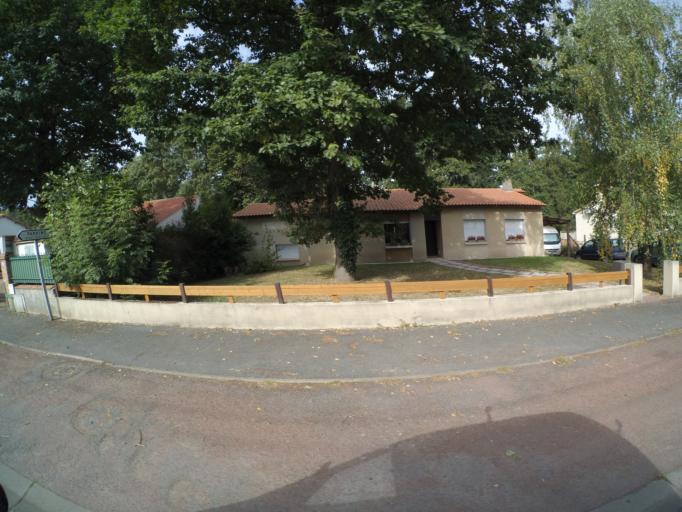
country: FR
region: Pays de la Loire
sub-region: Departement de Maine-et-Loire
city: Villedieu-la-Blouere
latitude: 47.1532
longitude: -1.0577
